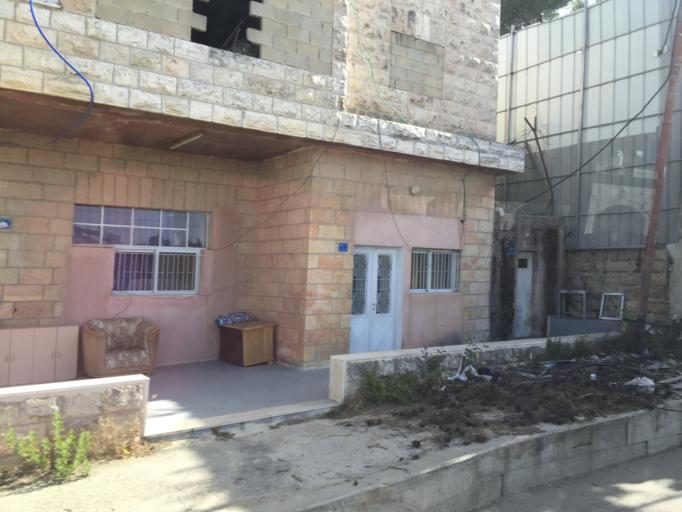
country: PS
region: West Bank
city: Bayt Jala
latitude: 31.7159
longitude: 35.1779
